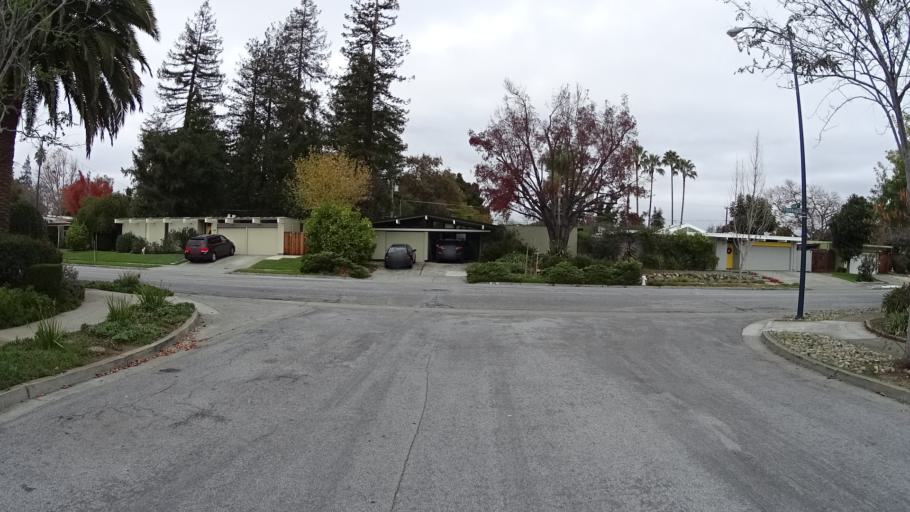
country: US
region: California
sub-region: Santa Clara County
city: Sunnyvale
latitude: 37.3556
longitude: -122.0406
